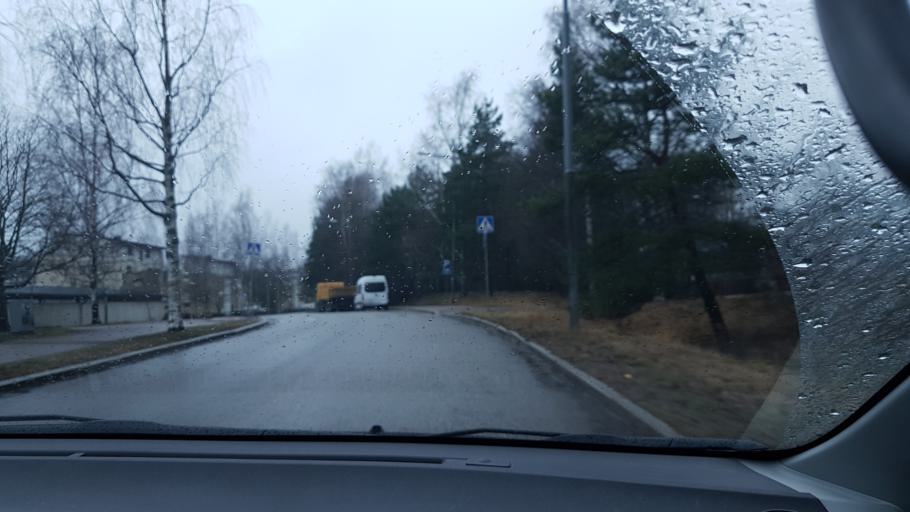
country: FI
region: Uusimaa
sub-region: Helsinki
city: Vantaa
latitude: 60.2324
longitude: 25.0763
